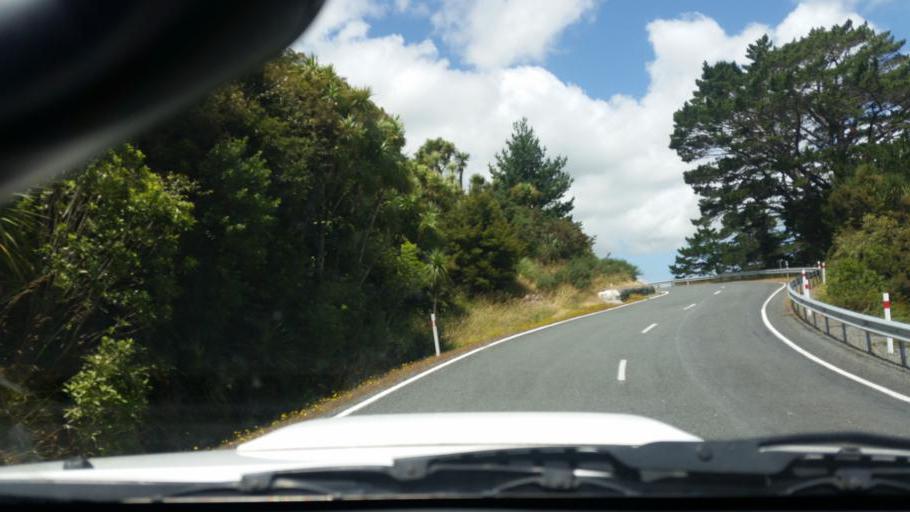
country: NZ
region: Northland
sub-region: Whangarei
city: Ruakaka
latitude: -36.0766
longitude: 174.2563
